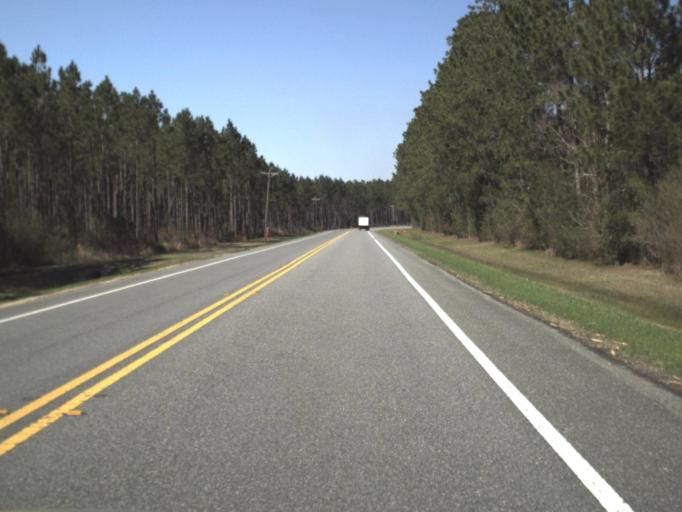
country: US
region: Florida
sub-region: Calhoun County
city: Blountstown
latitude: 30.3990
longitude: -85.0867
